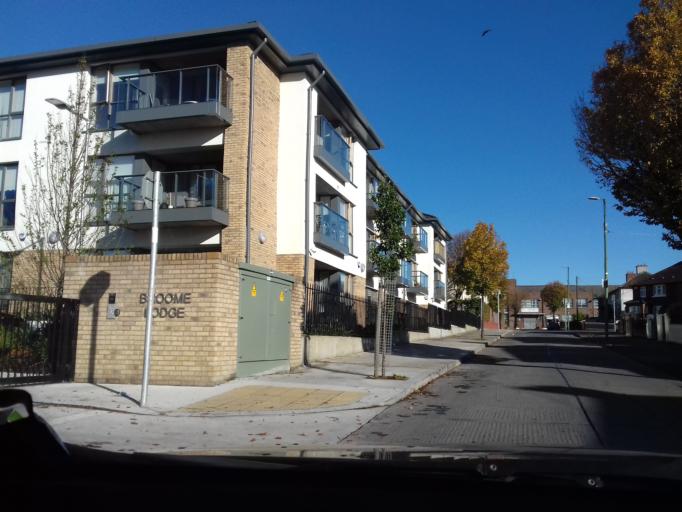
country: IE
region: Leinster
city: Cabra
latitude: 53.3673
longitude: -6.2946
